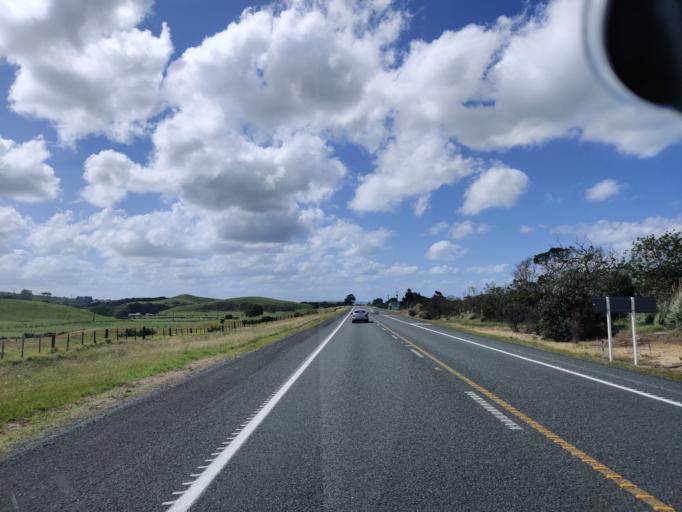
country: NZ
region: Northland
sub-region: Whangarei
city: Ruakaka
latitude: -35.9317
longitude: 174.4549
